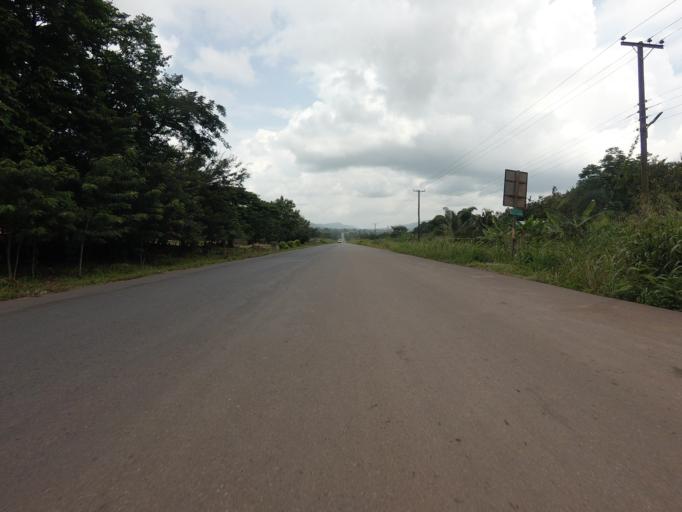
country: GH
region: Volta
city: Ho
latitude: 6.6217
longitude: 0.3078
